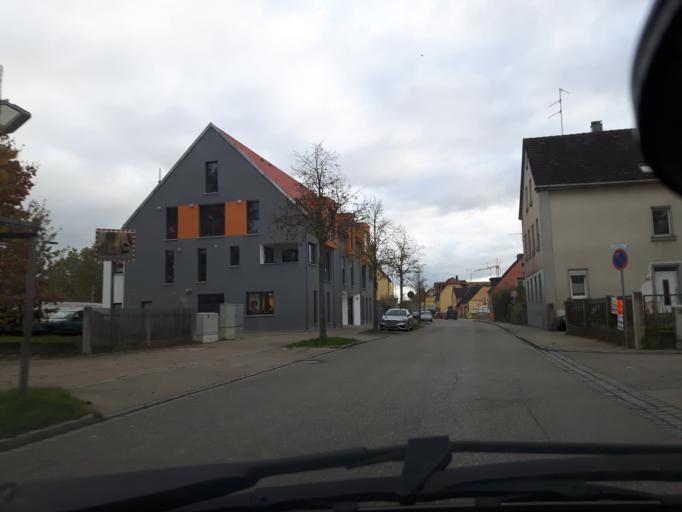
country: DE
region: Bavaria
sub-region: Regierungsbezirk Mittelfranken
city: Gunzenhausen
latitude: 49.1106
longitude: 10.7568
